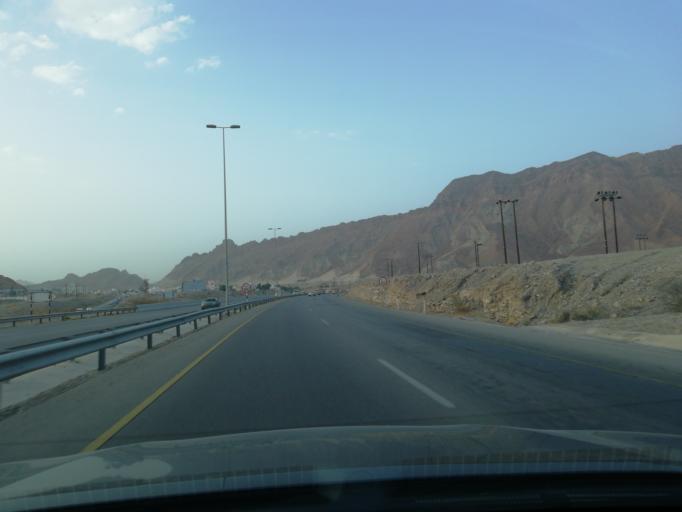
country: OM
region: Muhafazat ad Dakhiliyah
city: Bidbid
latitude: 23.4383
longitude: 58.1203
